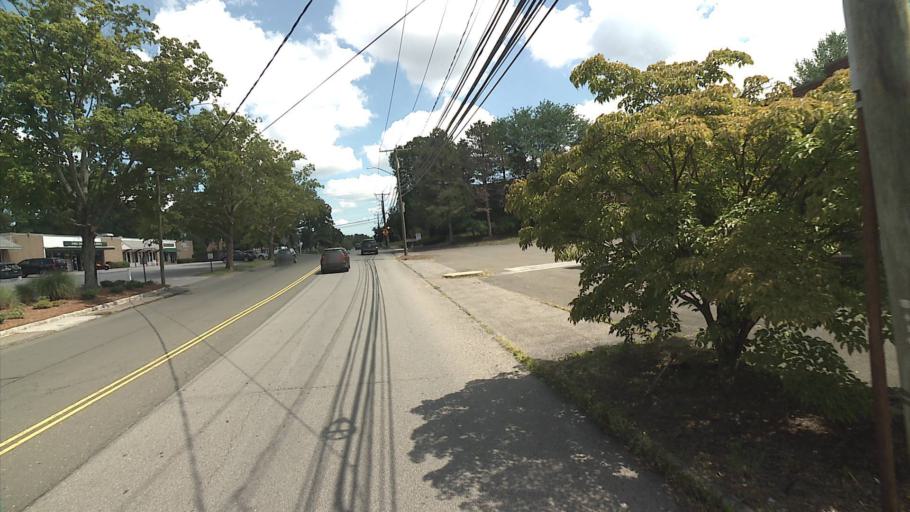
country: US
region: Connecticut
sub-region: Fairfield County
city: Darien
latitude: 41.0861
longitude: -73.4610
